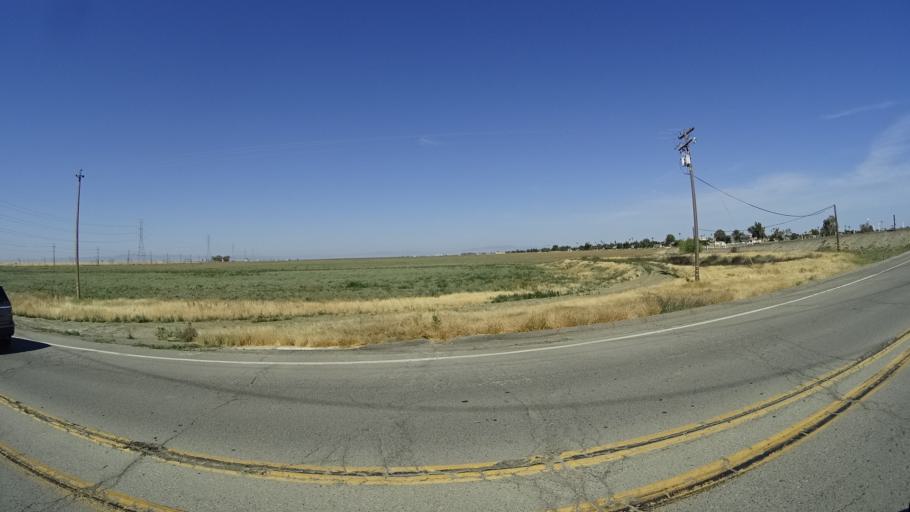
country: US
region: California
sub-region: Kings County
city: Lemoore Station
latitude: 36.2535
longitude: -119.8693
